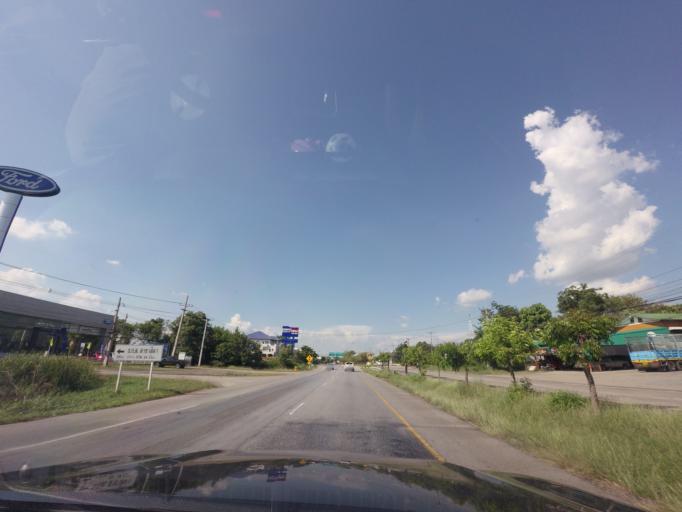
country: TH
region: Nakhon Ratchasima
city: Sida
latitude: 15.5440
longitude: 102.5472
